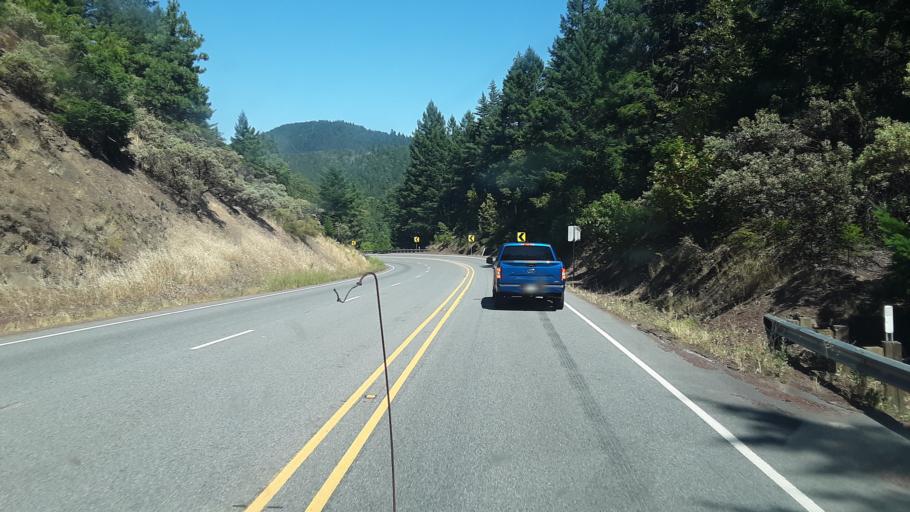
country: US
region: Oregon
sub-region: Josephine County
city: Cave Junction
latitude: 42.3384
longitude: -123.5801
